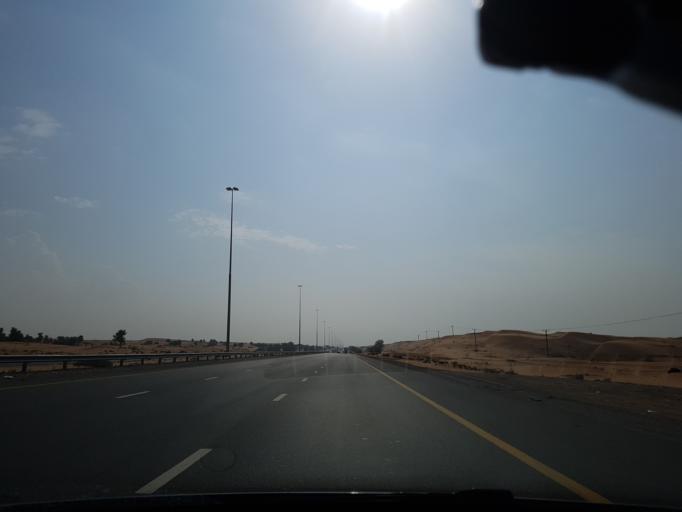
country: AE
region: Umm al Qaywayn
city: Umm al Qaywayn
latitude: 25.5143
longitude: 55.7072
